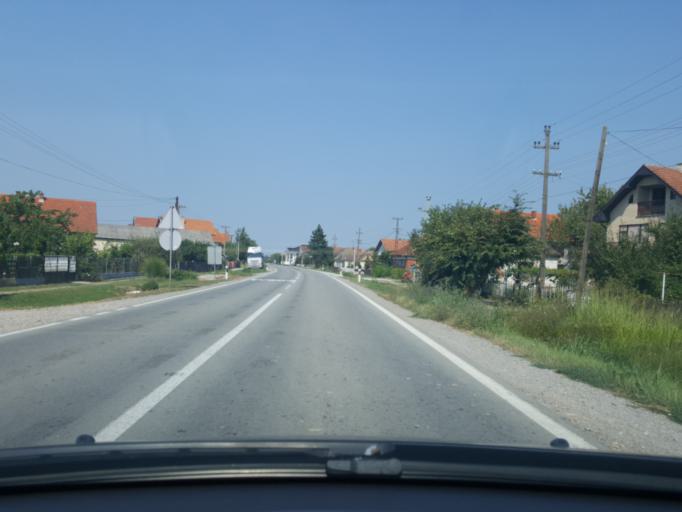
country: RS
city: Lipolist
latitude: 44.7401
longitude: 19.5225
